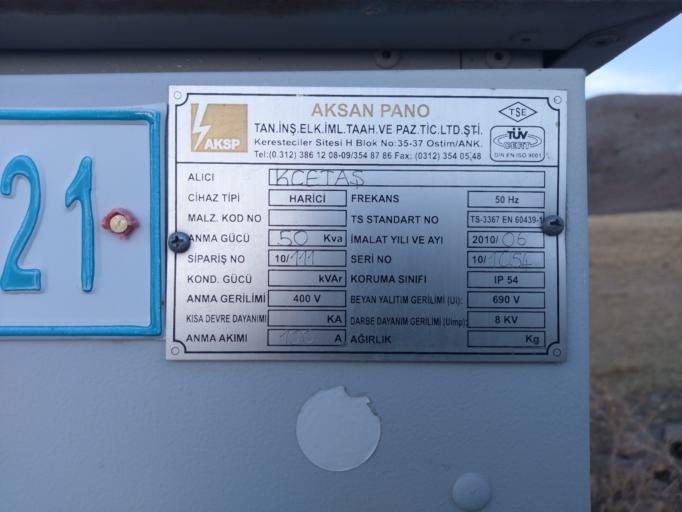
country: TR
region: Kayseri
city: Toklar
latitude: 38.4148
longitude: 36.0960
